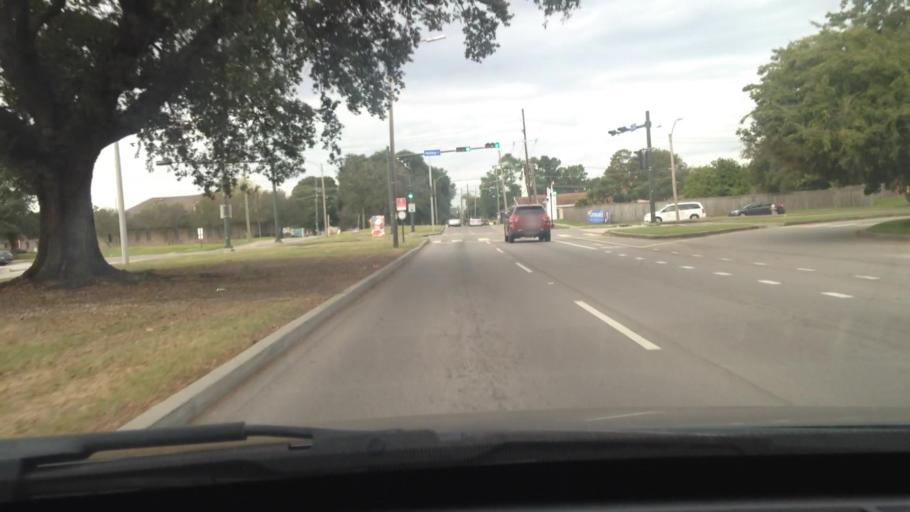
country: US
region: Louisiana
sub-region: Jefferson Parish
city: Terrytown
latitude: 29.9245
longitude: -90.0132
